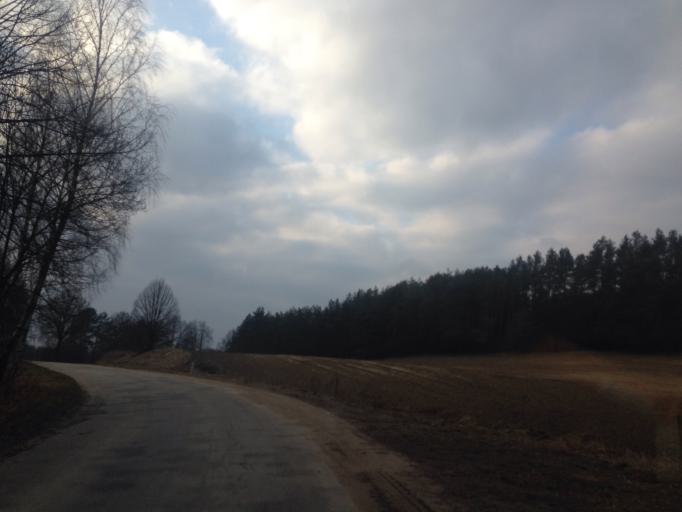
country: PL
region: Warmian-Masurian Voivodeship
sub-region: Powiat dzialdowski
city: Lidzbark
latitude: 53.3477
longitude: 19.7348
